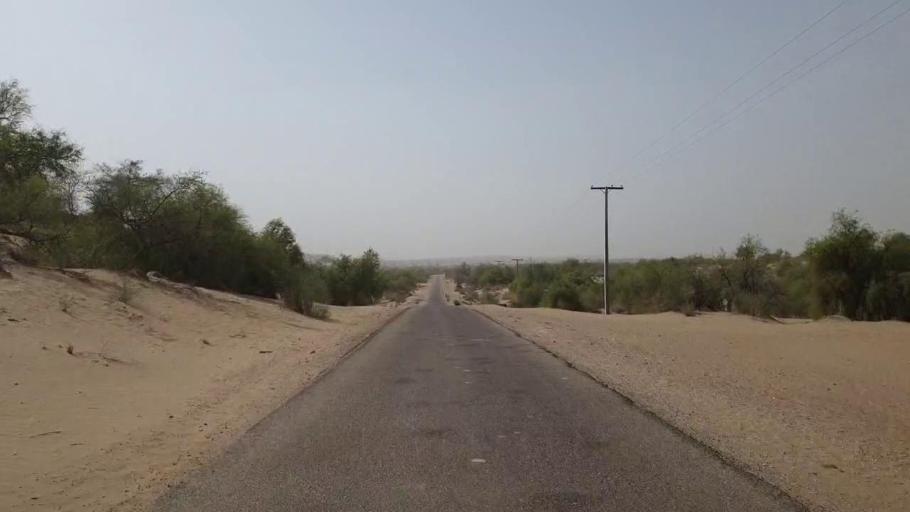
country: PK
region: Sindh
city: Mithi
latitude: 24.5999
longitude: 69.9240
